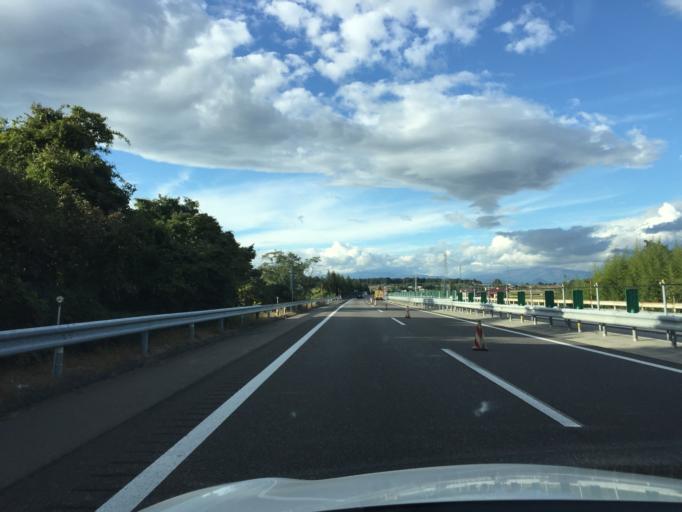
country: JP
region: Fukushima
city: Sukagawa
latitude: 37.3237
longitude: 140.3404
